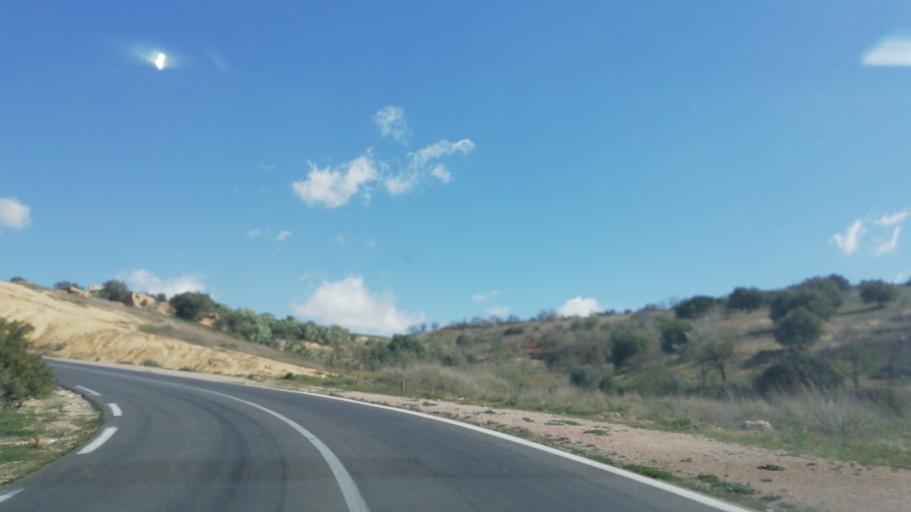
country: DZ
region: Mascara
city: Mascara
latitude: 35.4922
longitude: 0.1335
